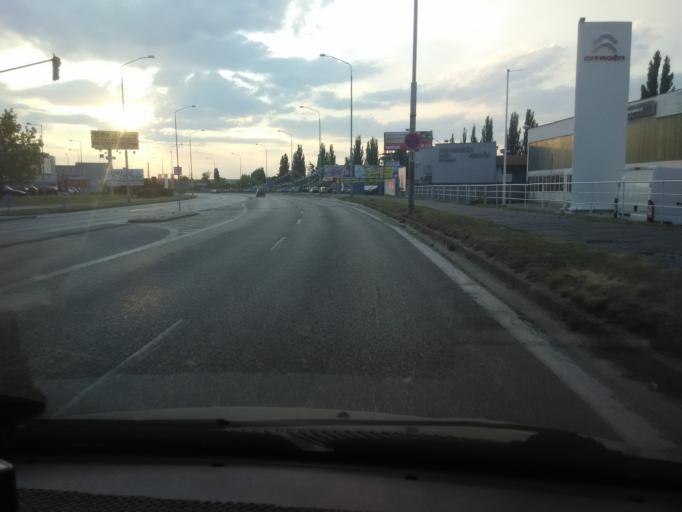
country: SK
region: Nitriansky
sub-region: Okres Nitra
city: Nitra
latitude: 48.3124
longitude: 18.0712
